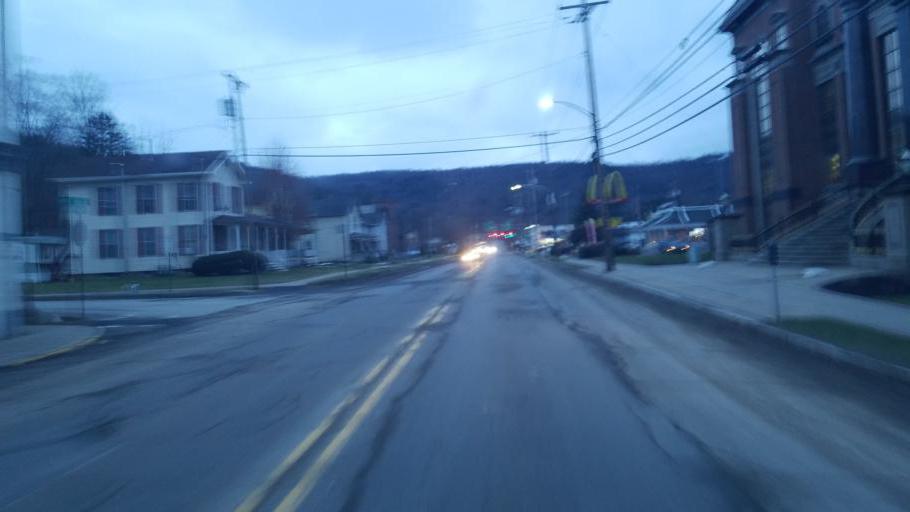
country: US
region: Pennsylvania
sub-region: Potter County
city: Coudersport
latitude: 41.7717
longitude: -78.0213
